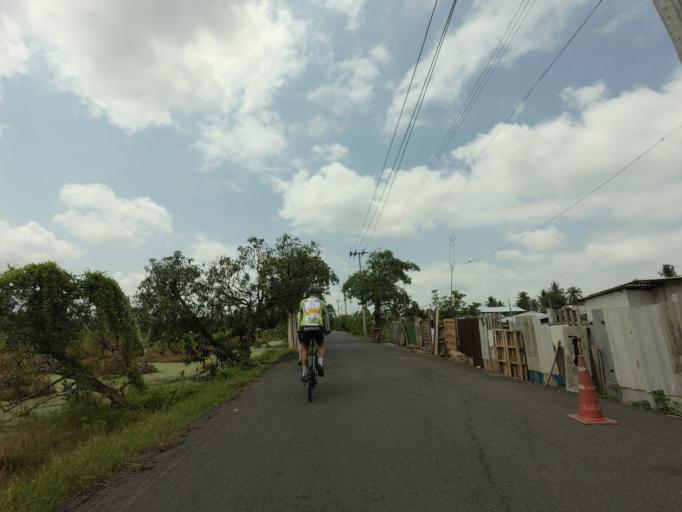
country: TH
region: Bangkok
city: Thung Khru
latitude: 13.6329
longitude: 100.4876
